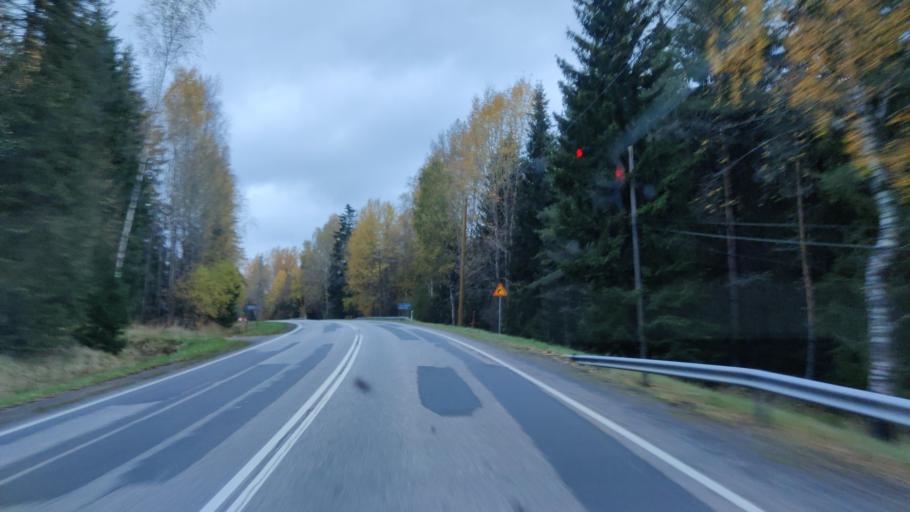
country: FI
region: Uusimaa
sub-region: Helsinki
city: Vihti
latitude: 60.3334
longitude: 24.2071
